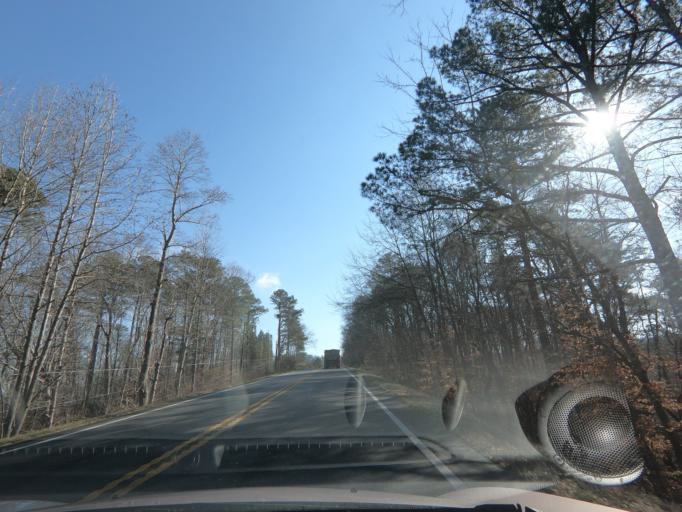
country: US
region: Georgia
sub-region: Cherokee County
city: Ball Ground
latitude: 34.2990
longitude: -84.2468
